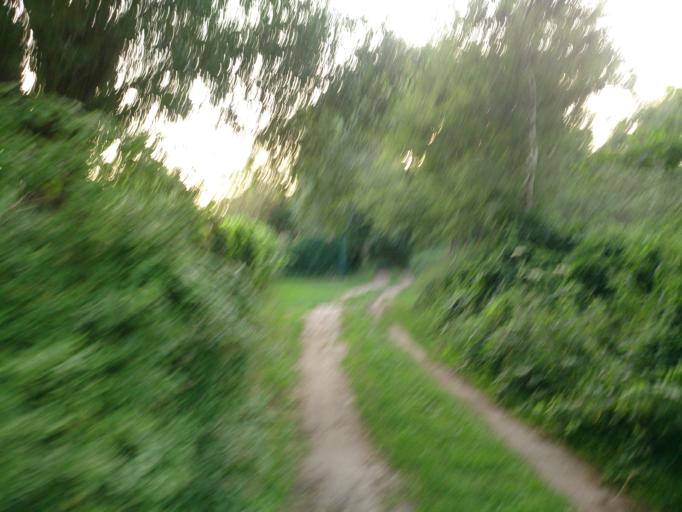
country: DE
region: Hamburg
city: Altona
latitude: 53.4799
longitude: 9.8962
